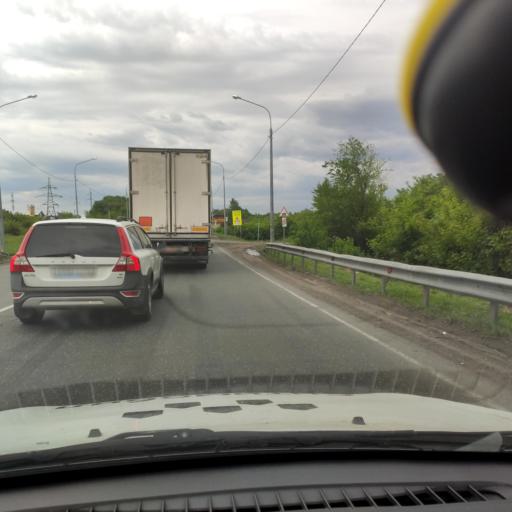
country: RU
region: Samara
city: Zhigulevsk
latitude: 53.3672
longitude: 49.4567
